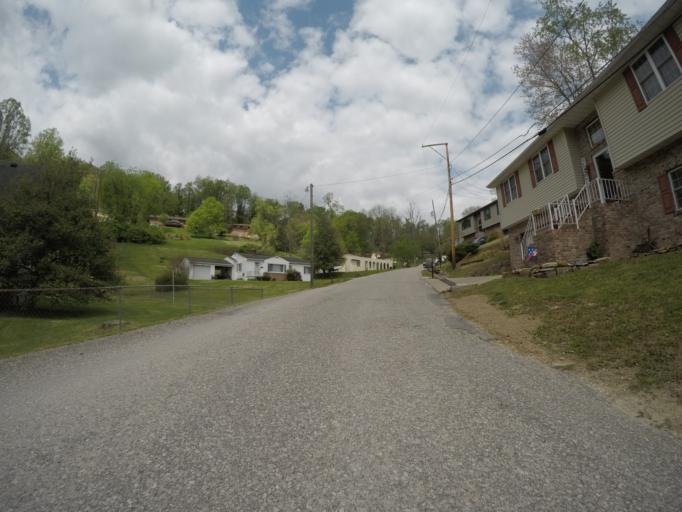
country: US
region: West Virginia
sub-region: Kanawha County
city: Charleston
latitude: 38.3837
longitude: -81.6052
